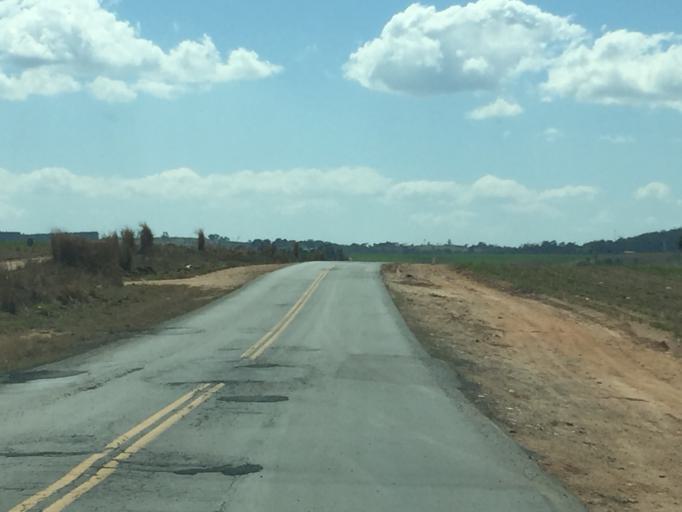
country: BR
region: Sao Paulo
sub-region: Moji-Guacu
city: Mogi-Gaucu
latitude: -22.3693
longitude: -46.8742
